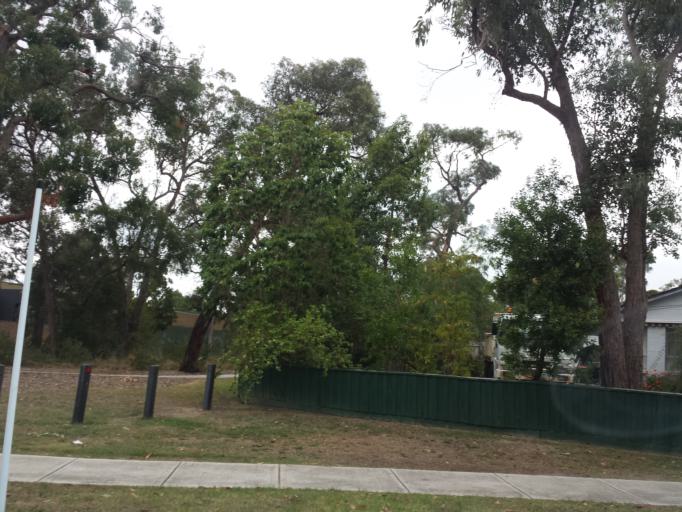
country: AU
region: Victoria
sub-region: Knox
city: Knoxfield
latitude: -37.8813
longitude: 145.2668
